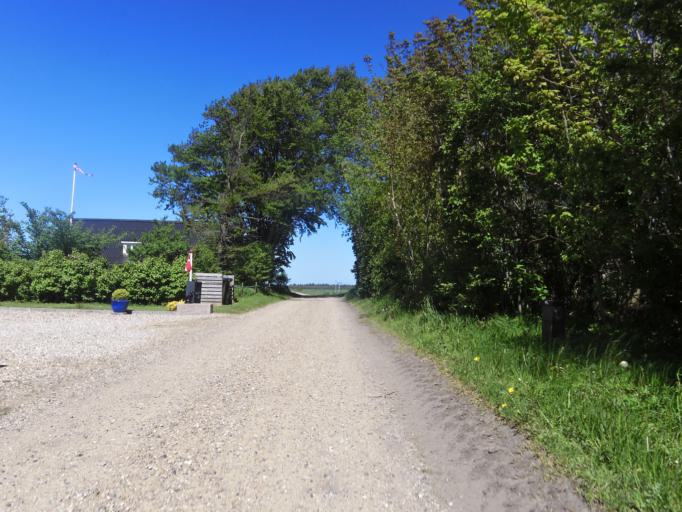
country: DK
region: South Denmark
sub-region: Tonder Kommune
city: Sherrebek
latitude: 55.2373
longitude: 8.7100
